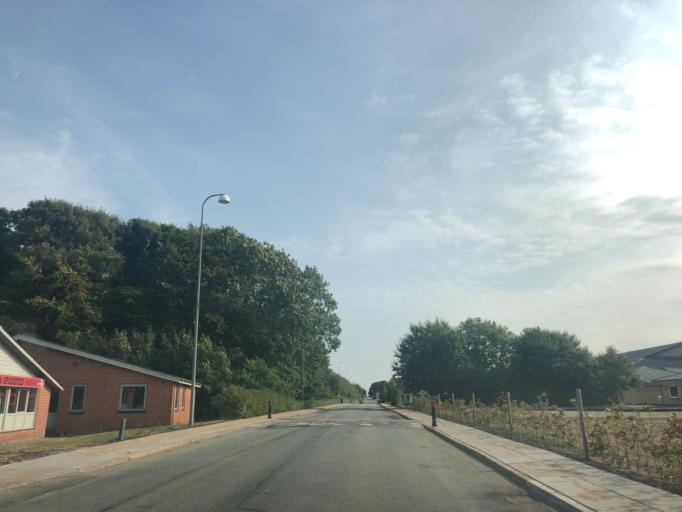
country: DK
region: Central Jutland
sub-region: Skive Kommune
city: Skive
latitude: 56.7017
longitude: 8.9807
